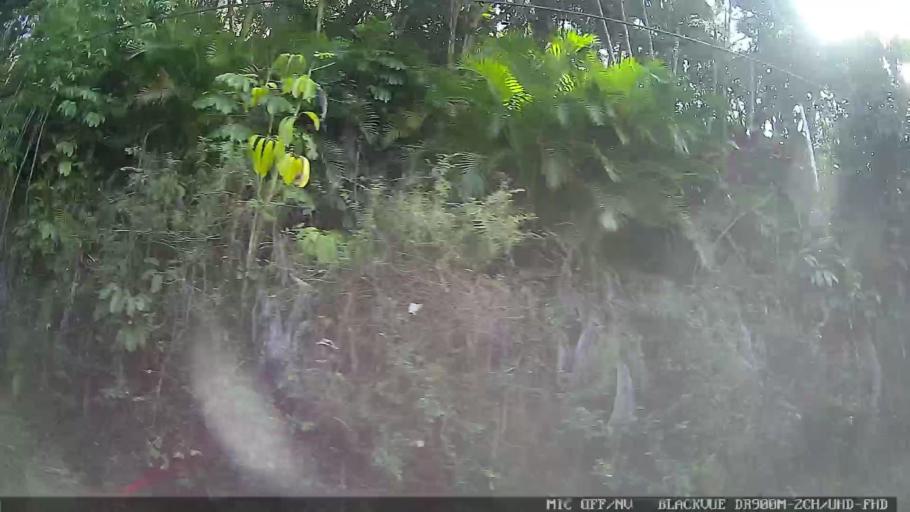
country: BR
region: Sao Paulo
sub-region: Guaruja
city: Guaruja
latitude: -23.9844
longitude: -46.1881
